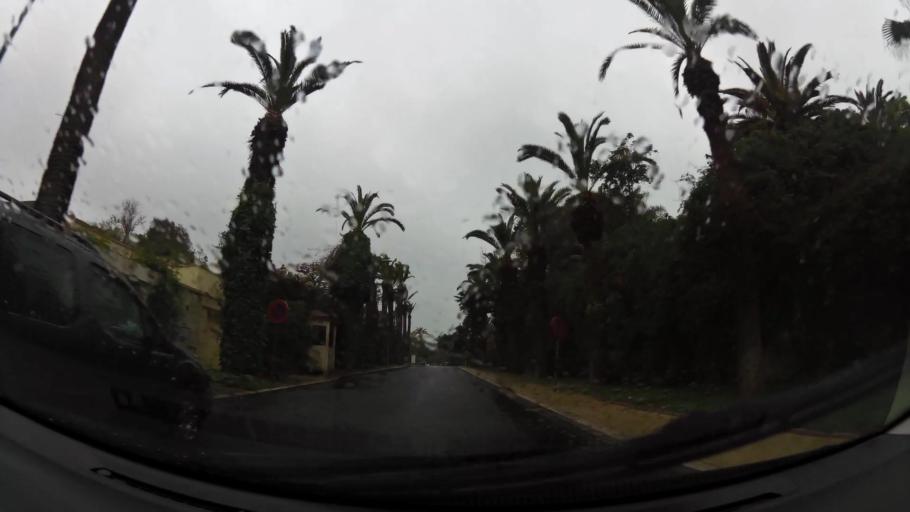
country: MA
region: Grand Casablanca
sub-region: Casablanca
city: Casablanca
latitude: 33.5865
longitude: -7.6620
